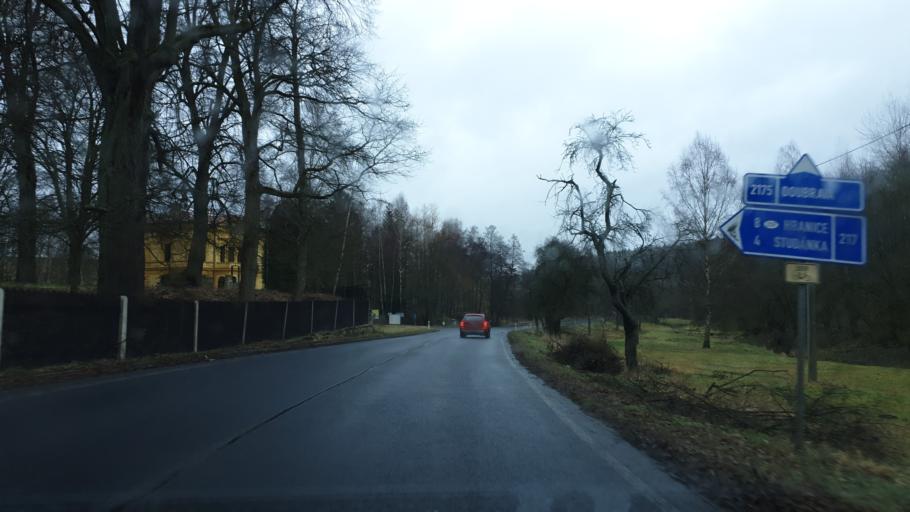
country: CZ
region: Karlovarsky
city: As
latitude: 50.2391
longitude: 12.1859
